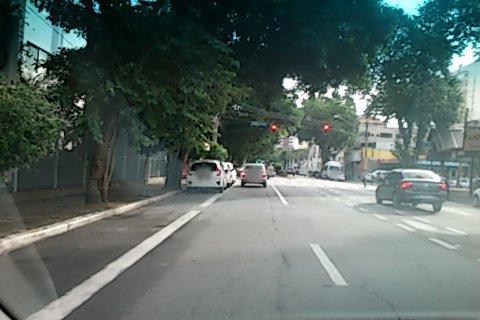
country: BR
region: Sao Paulo
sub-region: Sao Jose Dos Campos
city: Sao Jose dos Campos
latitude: -23.1972
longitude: -45.8948
